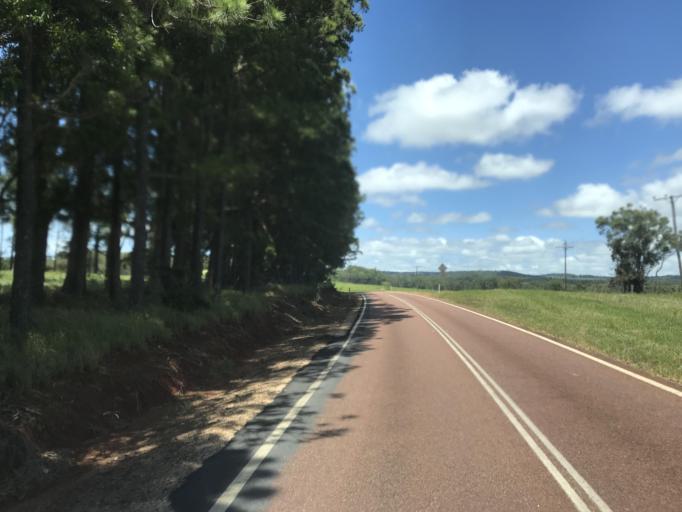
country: AU
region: Queensland
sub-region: Tablelands
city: Ravenshoe
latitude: -17.5292
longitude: 145.4539
